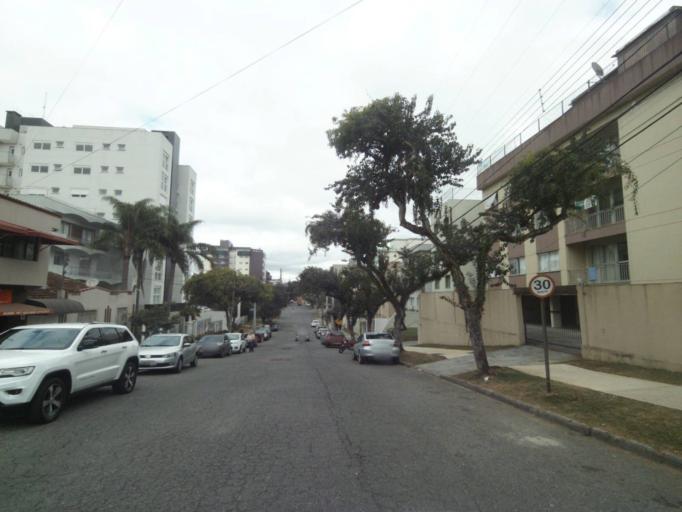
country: BR
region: Parana
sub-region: Curitiba
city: Curitiba
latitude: -25.4621
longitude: -49.2859
